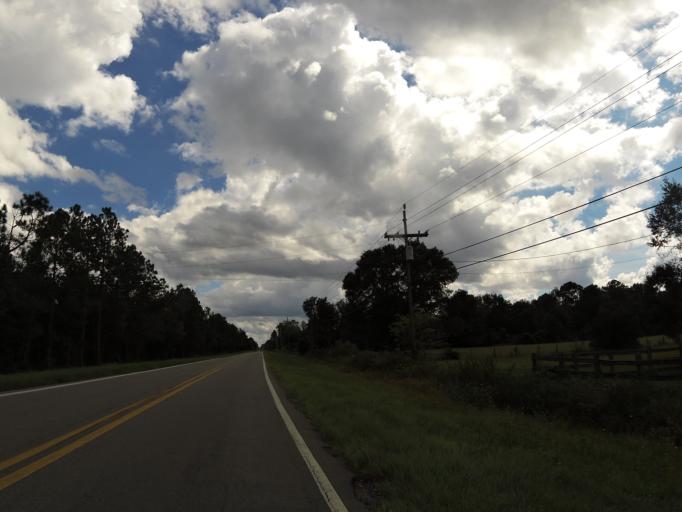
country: US
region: Florida
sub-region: Saint Johns County
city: Saint Augustine
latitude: 29.8996
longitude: -81.4949
